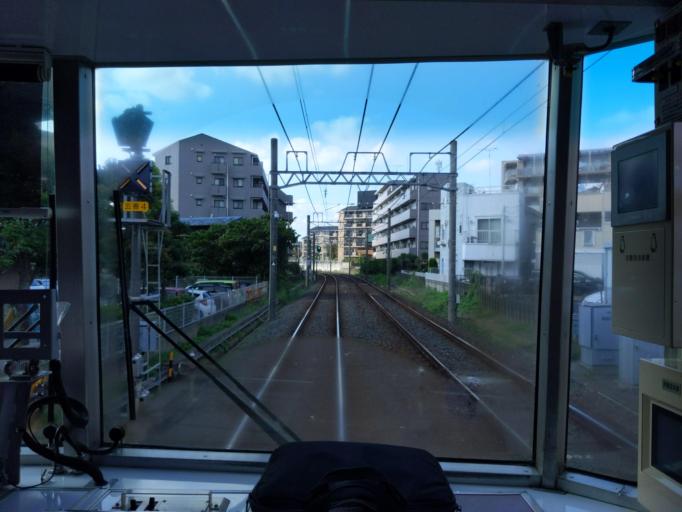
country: JP
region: Chiba
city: Kashiwa
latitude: 35.7910
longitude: 139.9750
